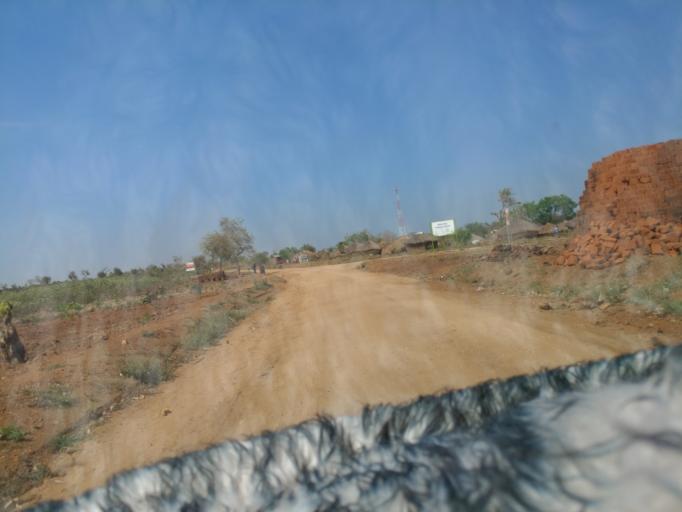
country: UG
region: Northern Region
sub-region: Yumbe District
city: Yumbe
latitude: 3.3914
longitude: 31.3384
